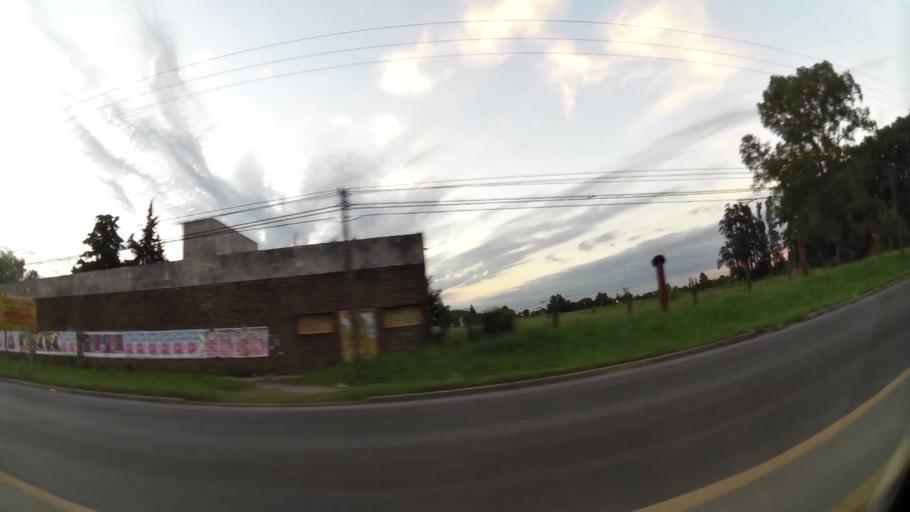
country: AR
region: Buenos Aires
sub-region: Partido de Merlo
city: Merlo
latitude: -34.6740
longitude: -58.7516
